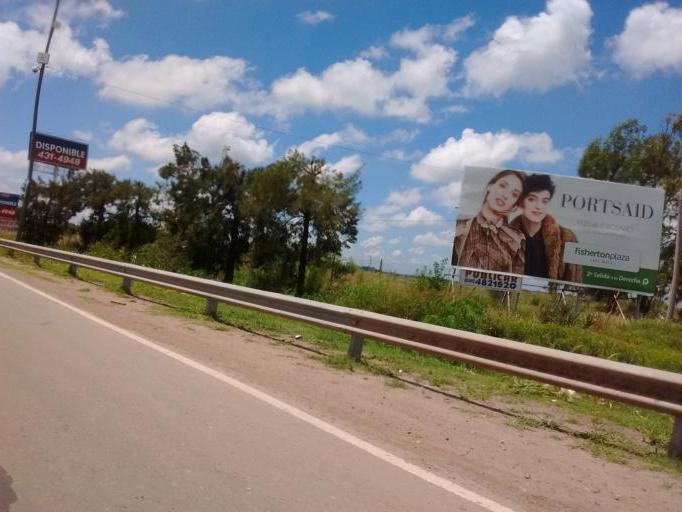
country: AR
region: Santa Fe
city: Funes
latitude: -32.9242
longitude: -60.7819
